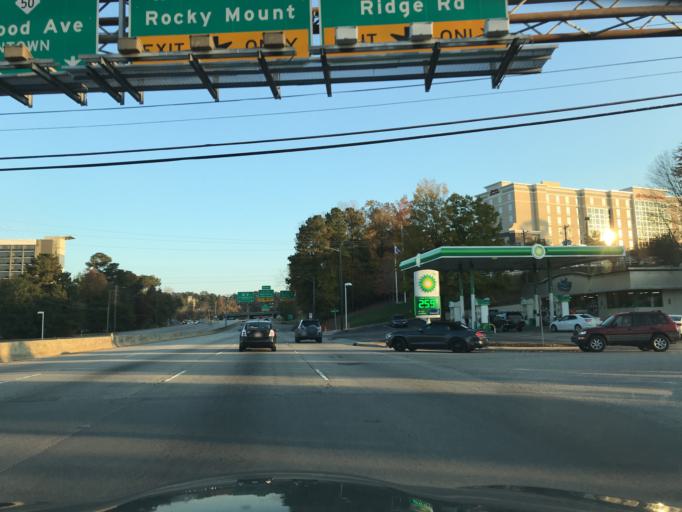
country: US
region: North Carolina
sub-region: Wake County
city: West Raleigh
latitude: 35.8379
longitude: -78.6737
